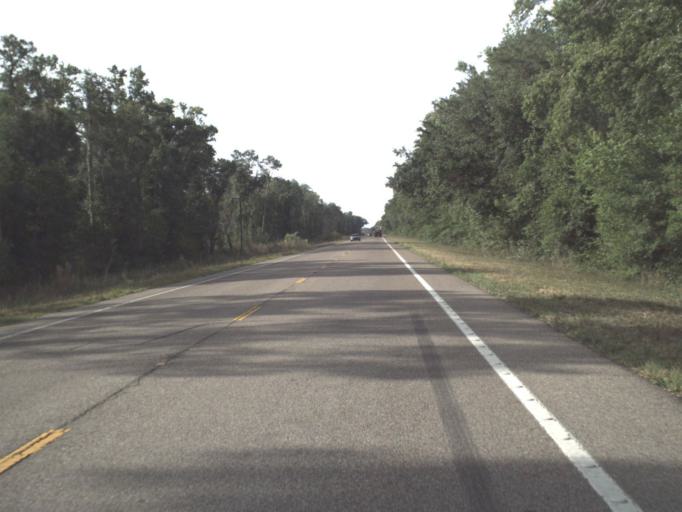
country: US
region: Florida
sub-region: Hernando County
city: Ridge Manor
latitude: 28.5277
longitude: -82.0546
